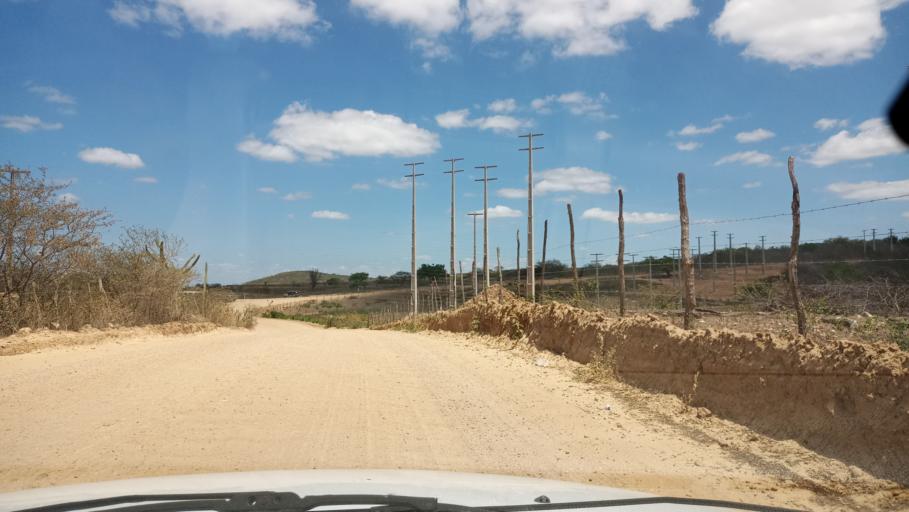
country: BR
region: Rio Grande do Norte
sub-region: Sao Paulo Do Potengi
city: Sao Paulo do Potengi
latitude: -5.7889
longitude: -35.9167
